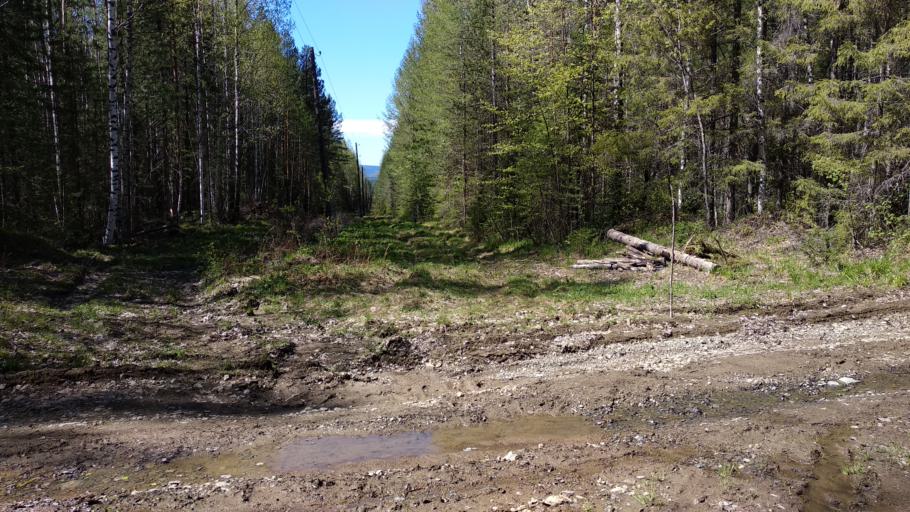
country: RU
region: Sverdlovsk
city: Karpinsk
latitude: 59.6939
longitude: 59.6717
